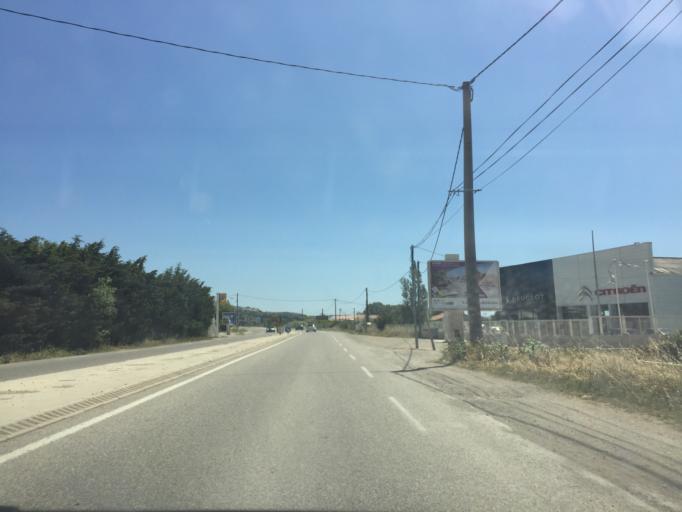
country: FR
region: Provence-Alpes-Cote d'Azur
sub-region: Departement des Bouches-du-Rhone
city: Rognac
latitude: 43.4892
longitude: 5.2197
